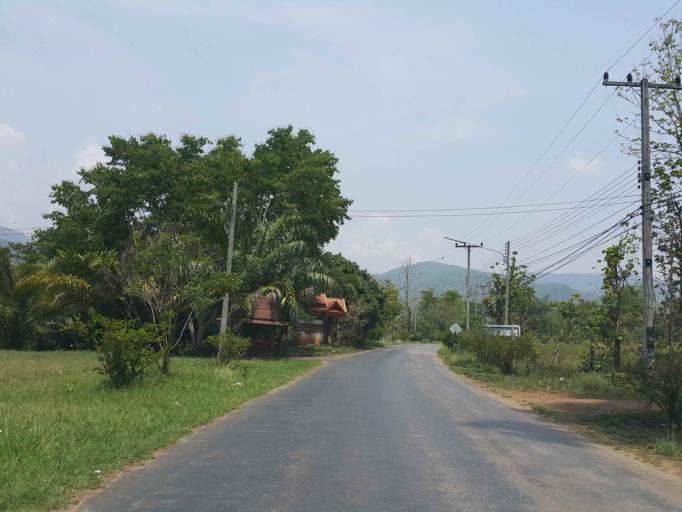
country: TH
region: Chiang Mai
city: Mae Taeng
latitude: 19.1433
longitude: 98.8657
